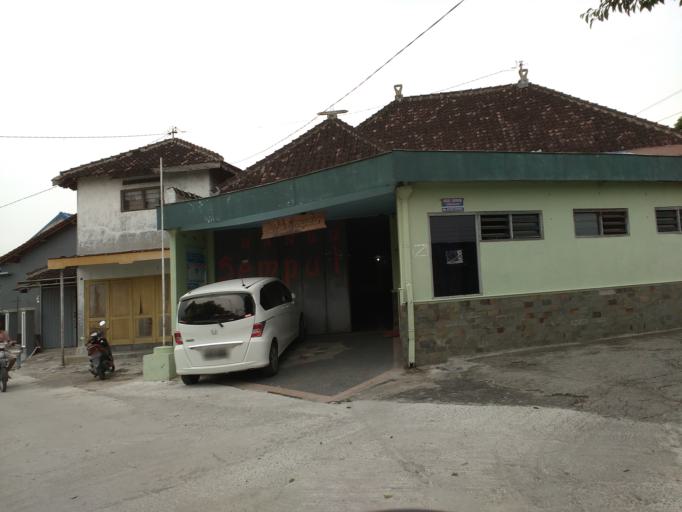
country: ID
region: Central Java
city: Delanggu
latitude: -7.5955
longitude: 110.6464
